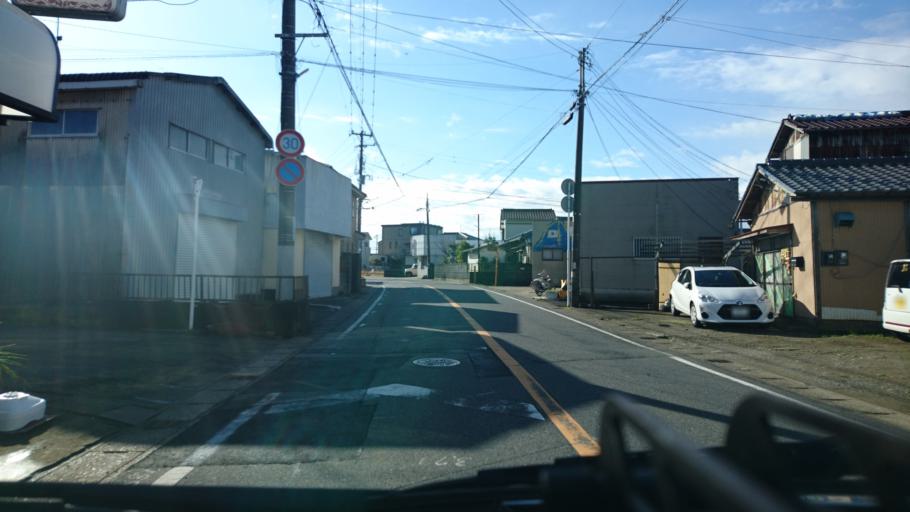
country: JP
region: Chiba
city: Kisarazu
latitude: 35.3753
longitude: 139.9229
